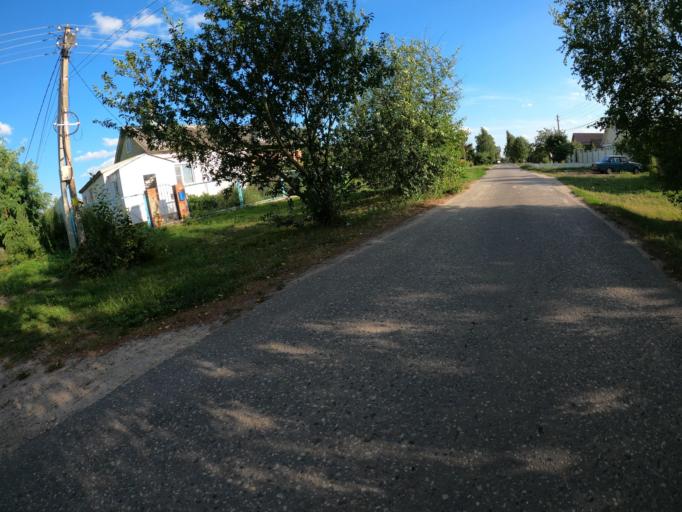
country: RU
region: Moskovskaya
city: Raduzhnyy
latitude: 55.1509
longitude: 38.7368
